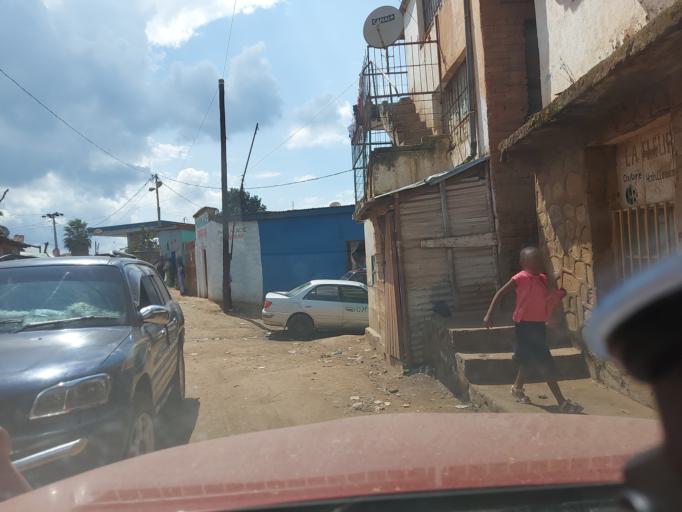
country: RW
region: Western Province
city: Cyangugu
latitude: -2.5012
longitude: 28.8810
